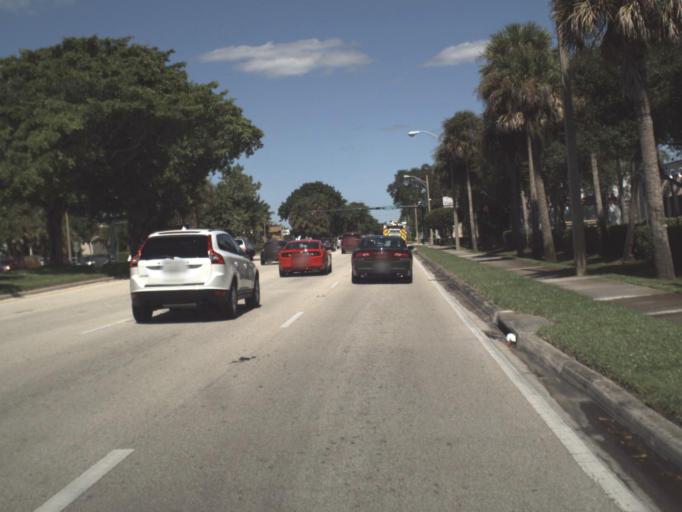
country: US
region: Florida
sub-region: Collier County
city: Naples
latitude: 26.1730
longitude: -81.7995
